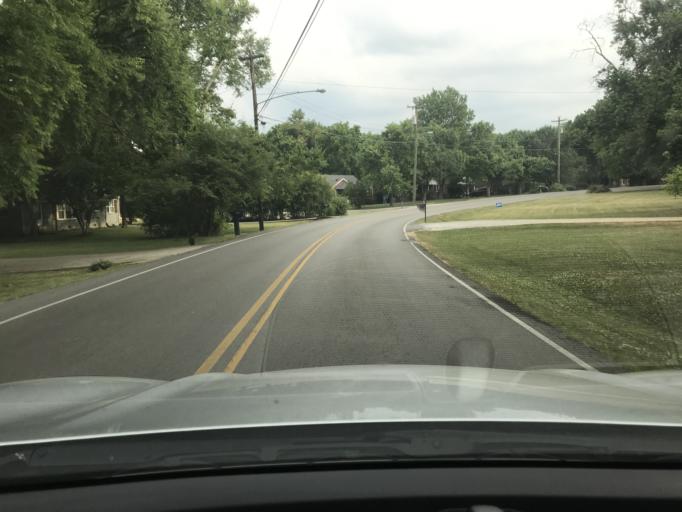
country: US
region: Tennessee
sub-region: Davidson County
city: Goodlettsville
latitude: 36.3085
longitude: -86.7065
